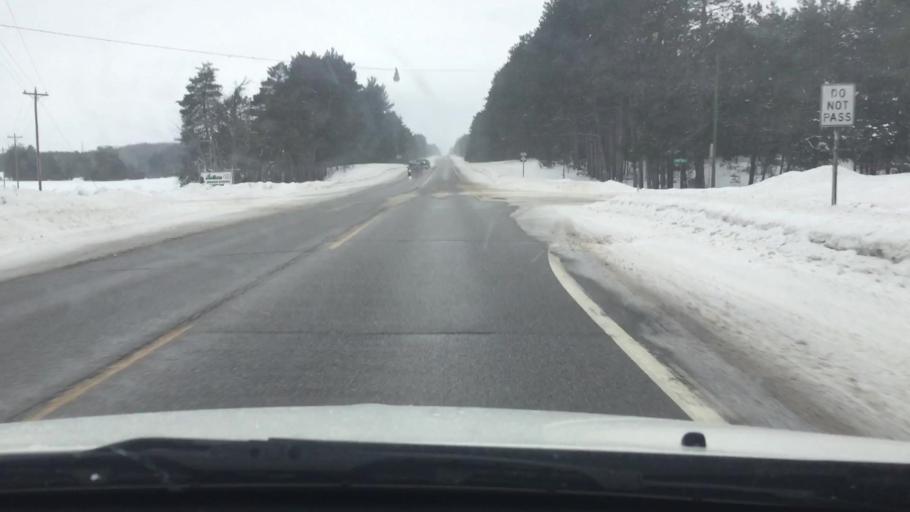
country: US
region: Michigan
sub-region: Otsego County
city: Gaylord
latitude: 45.0619
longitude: -84.8162
